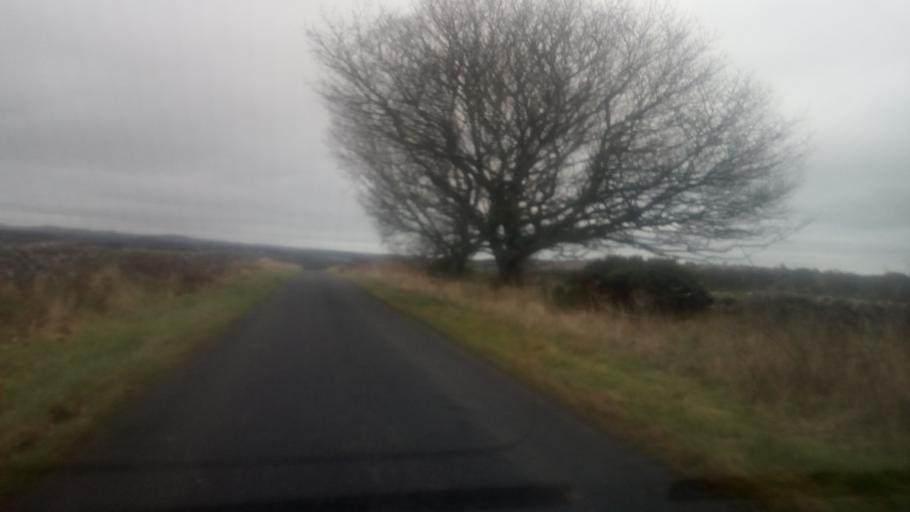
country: GB
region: Scotland
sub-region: The Scottish Borders
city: Kelso
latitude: 55.5560
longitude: -2.4848
